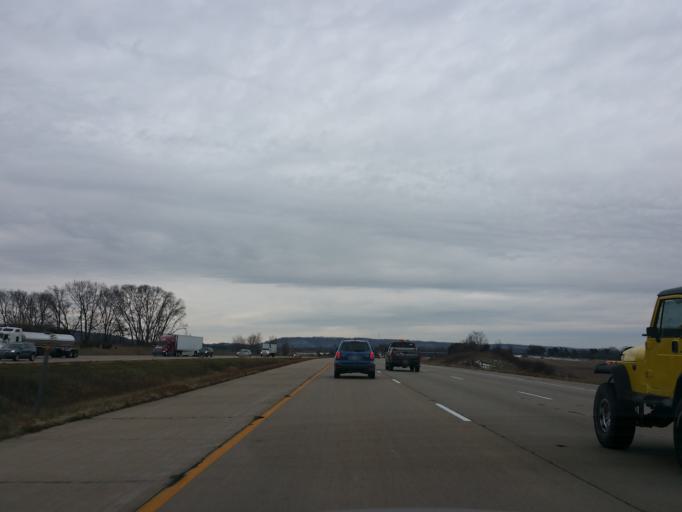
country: US
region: Wisconsin
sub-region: Columbia County
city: Poynette
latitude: 43.4150
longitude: -89.4710
